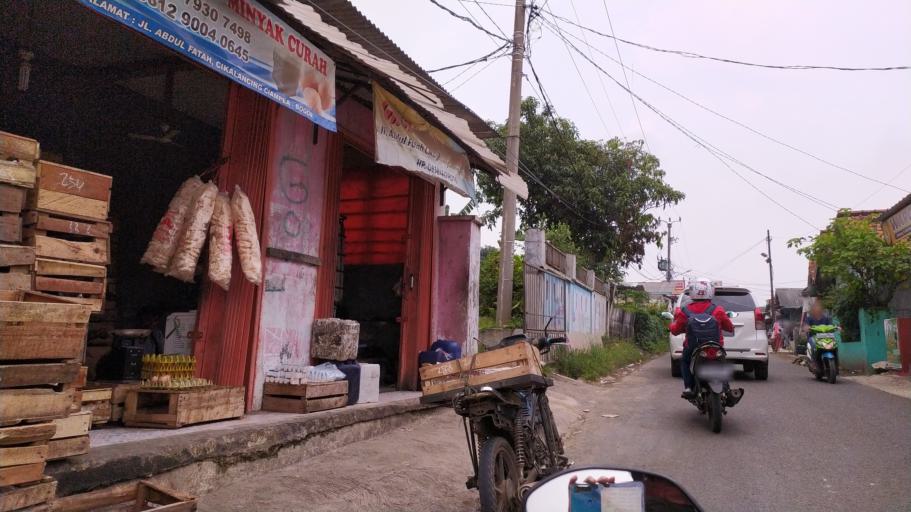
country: ID
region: West Java
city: Ciampea
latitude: -6.5929
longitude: 106.7049
